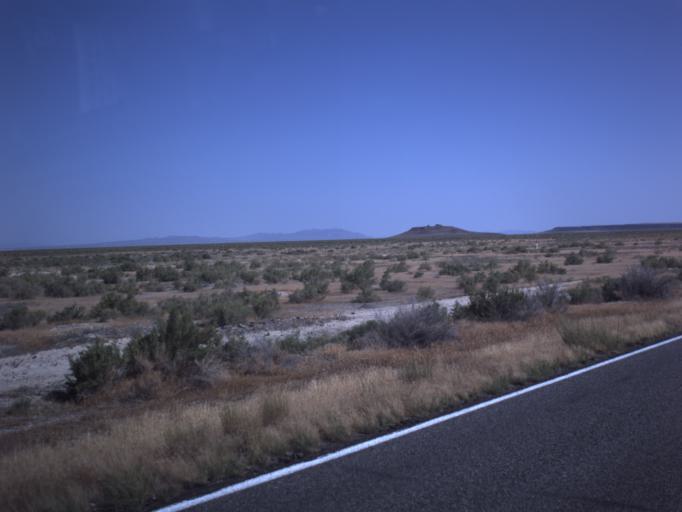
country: US
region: Utah
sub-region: Millard County
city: Delta
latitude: 39.0768
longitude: -112.7569
